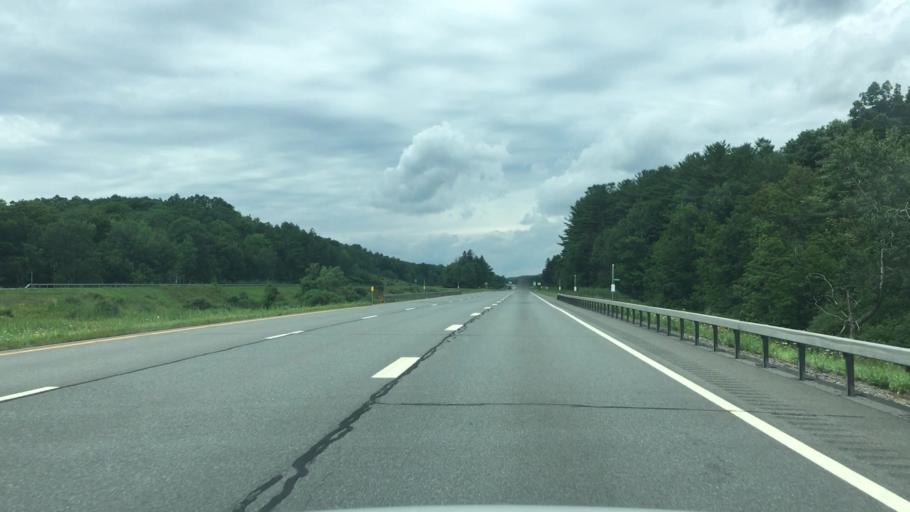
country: US
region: New York
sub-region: Albany County
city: Altamont
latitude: 42.7721
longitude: -74.0683
